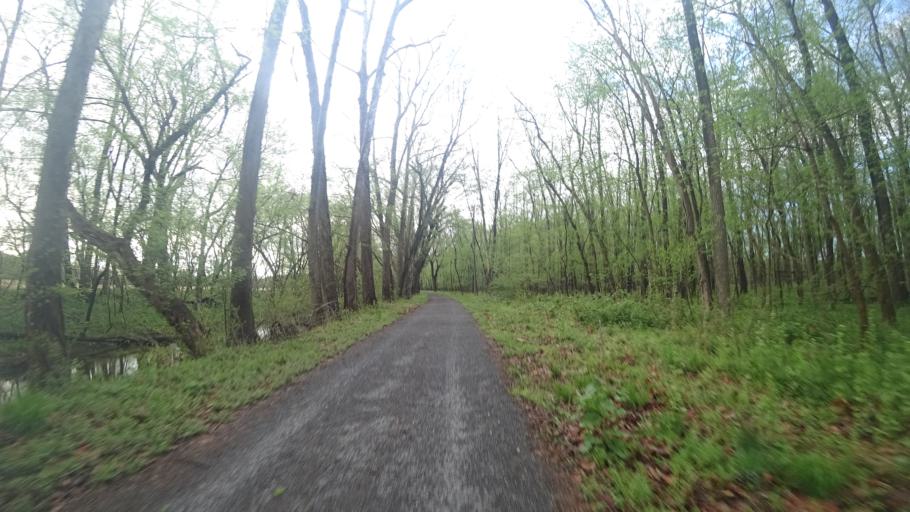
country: US
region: Virginia
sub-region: Loudoun County
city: Leesburg
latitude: 39.1255
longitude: -77.5137
